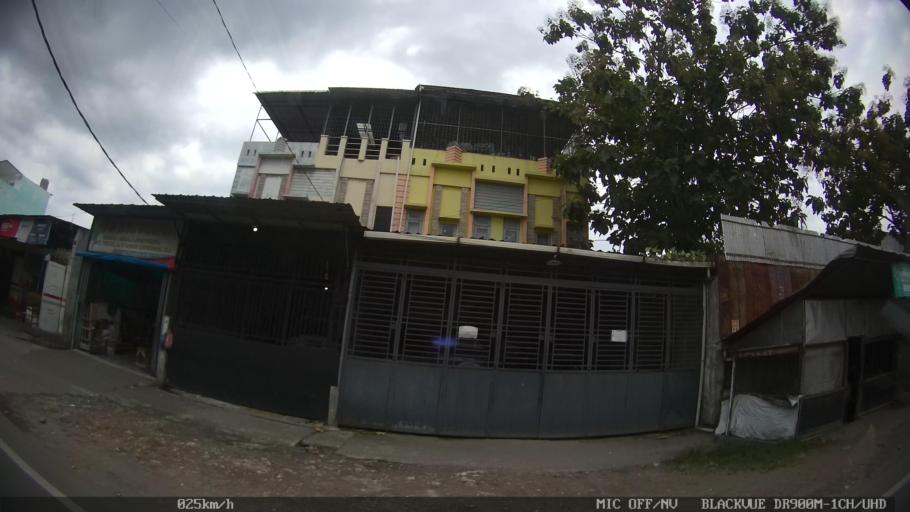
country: ID
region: North Sumatra
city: Sunggal
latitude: 3.6055
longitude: 98.6081
